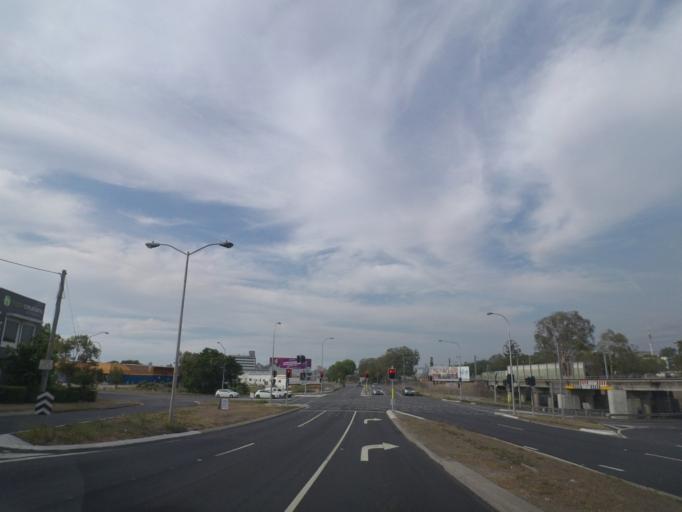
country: AU
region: Queensland
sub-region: Brisbane
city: Rocklea
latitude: -27.5419
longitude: 153.0115
